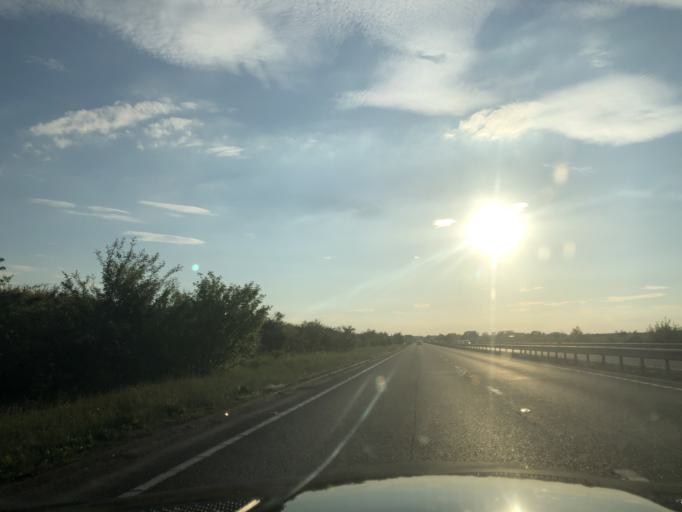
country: GB
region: England
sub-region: Bedford
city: Pertenhall
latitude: 52.3620
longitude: -0.4159
